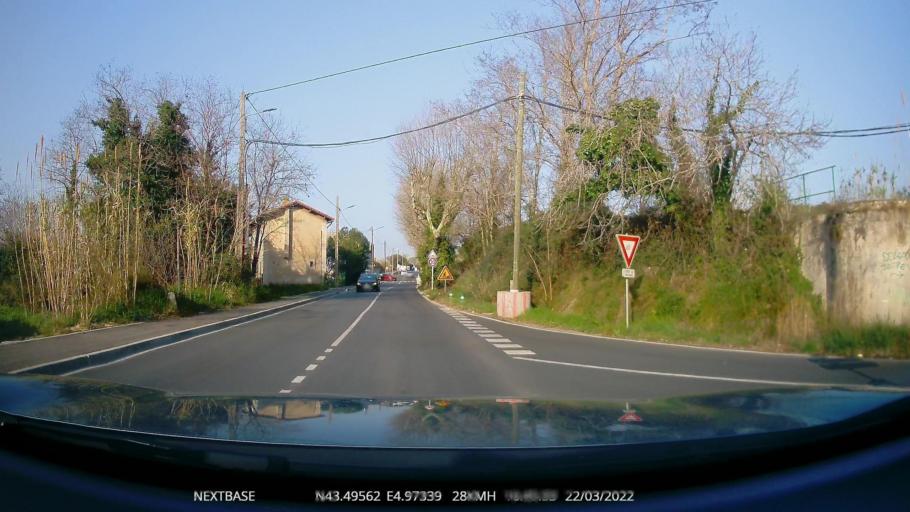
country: FR
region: Provence-Alpes-Cote d'Azur
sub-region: Departement des Bouches-du-Rhone
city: Istres
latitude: 43.4956
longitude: 4.9734
